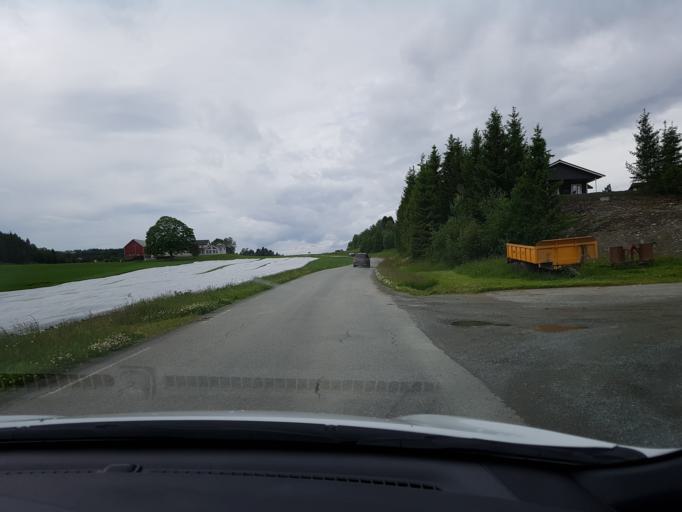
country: NO
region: Nord-Trondelag
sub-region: Frosta
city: Frosta
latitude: 63.6294
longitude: 10.7715
